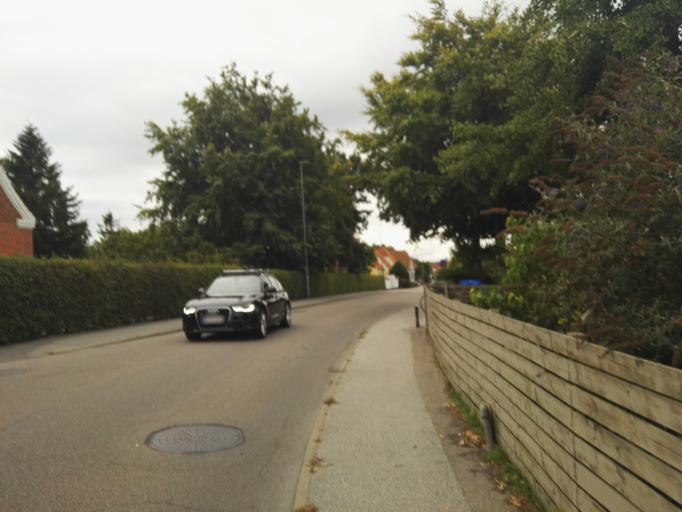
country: DK
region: Zealand
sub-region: Odsherred Kommune
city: Nykobing Sjaelland
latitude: 55.9281
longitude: 11.6689
